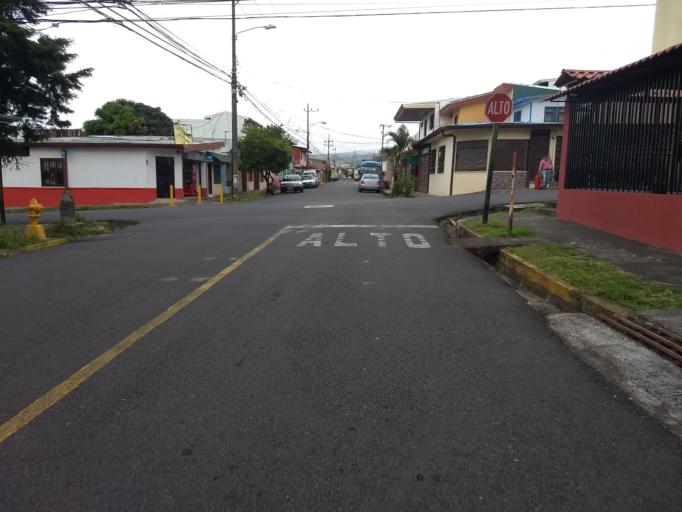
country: CR
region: San Jose
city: San Juan
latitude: 9.9614
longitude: -84.0810
